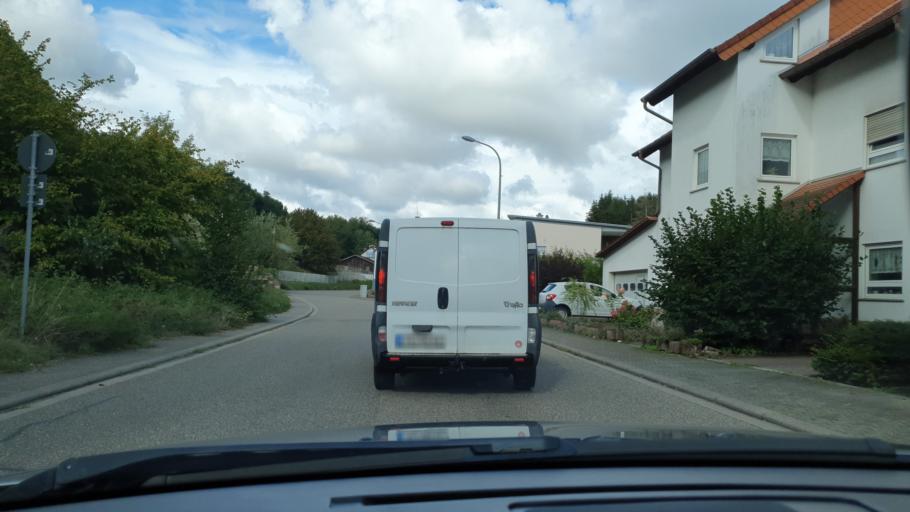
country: DE
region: Rheinland-Pfalz
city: Dellfeld
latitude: 49.2398
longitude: 7.4777
